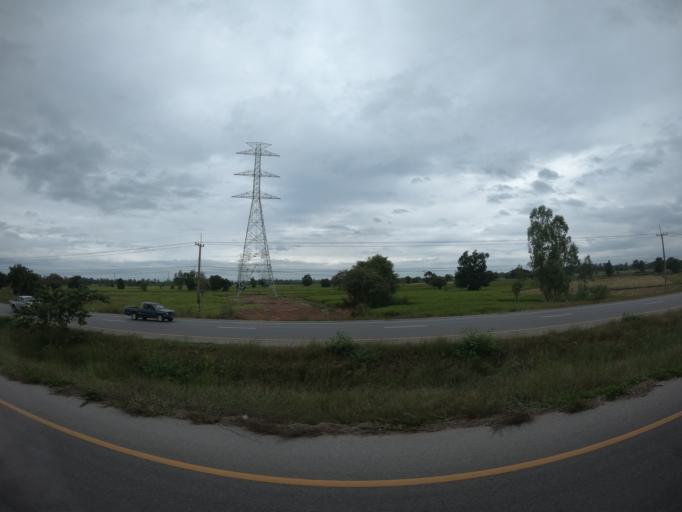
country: TH
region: Roi Et
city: Changhan
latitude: 16.0911
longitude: 103.5484
